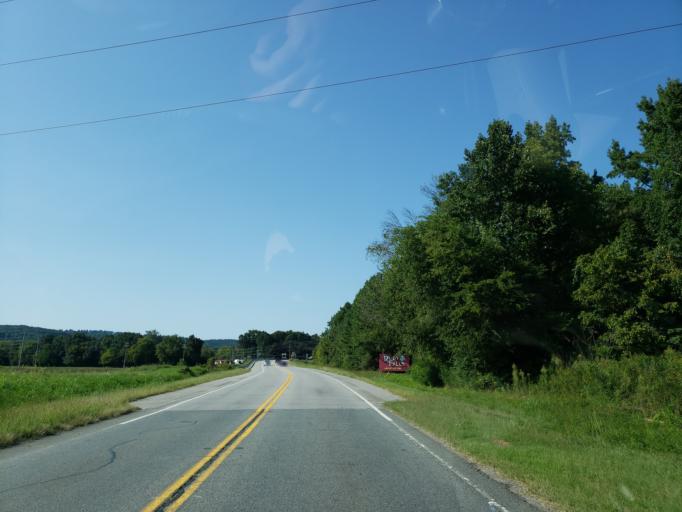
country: US
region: Georgia
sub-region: Catoosa County
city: Ringgold
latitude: 34.9024
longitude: -85.0760
